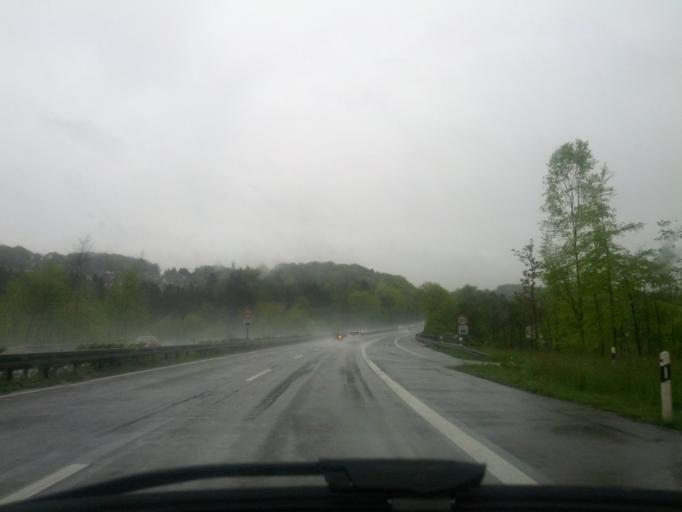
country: DE
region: North Rhine-Westphalia
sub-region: Regierungsbezirk Koln
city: Rosrath
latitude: 50.9486
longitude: 7.2174
